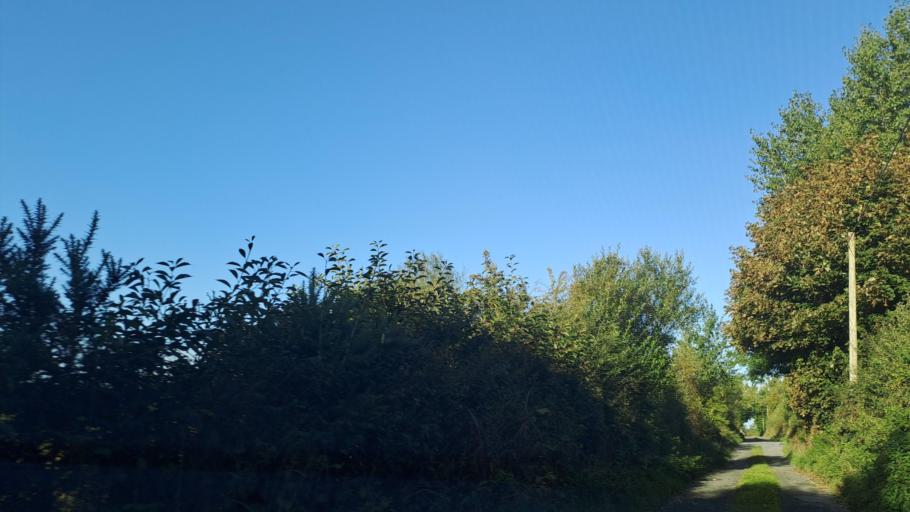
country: IE
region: Ulster
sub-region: An Cabhan
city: Kingscourt
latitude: 53.9860
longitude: -6.8349
